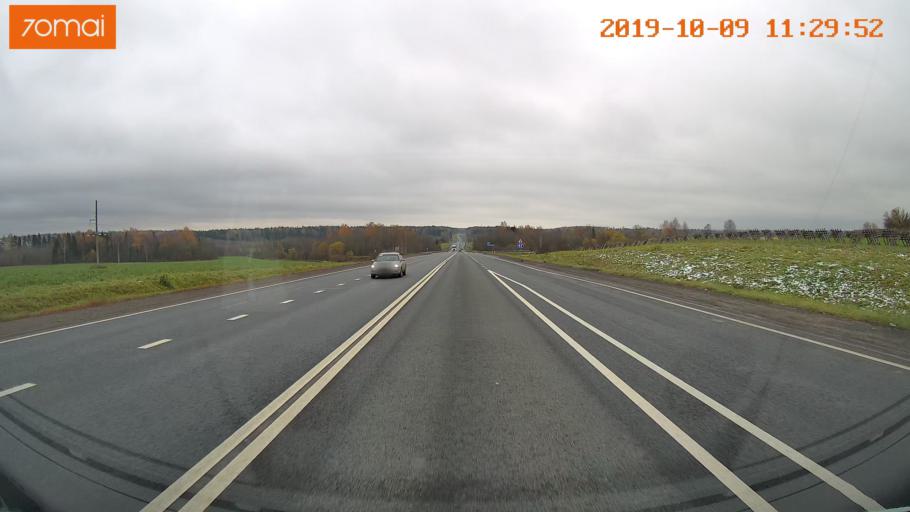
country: RU
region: Vologda
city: Vologda
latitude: 59.0587
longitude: 40.0626
